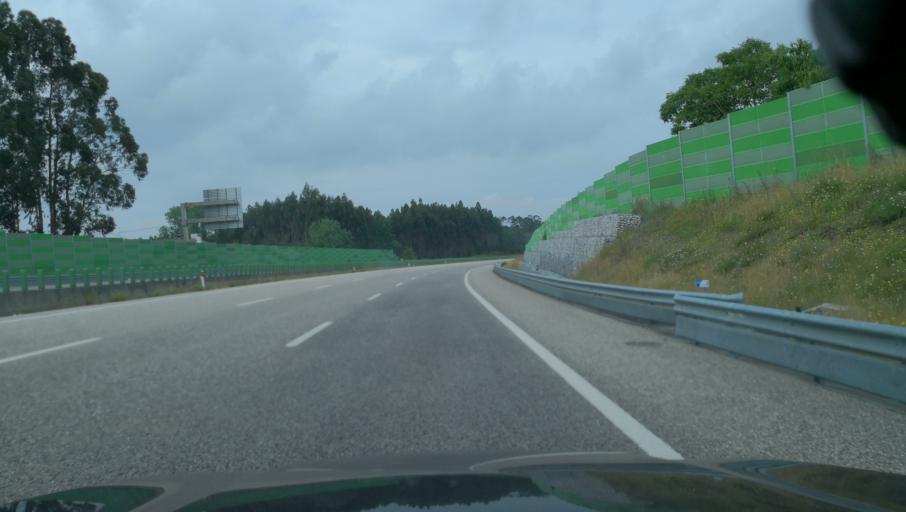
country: PT
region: Leiria
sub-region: Leiria
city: Monte Redondo
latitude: 39.9266
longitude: -8.7826
